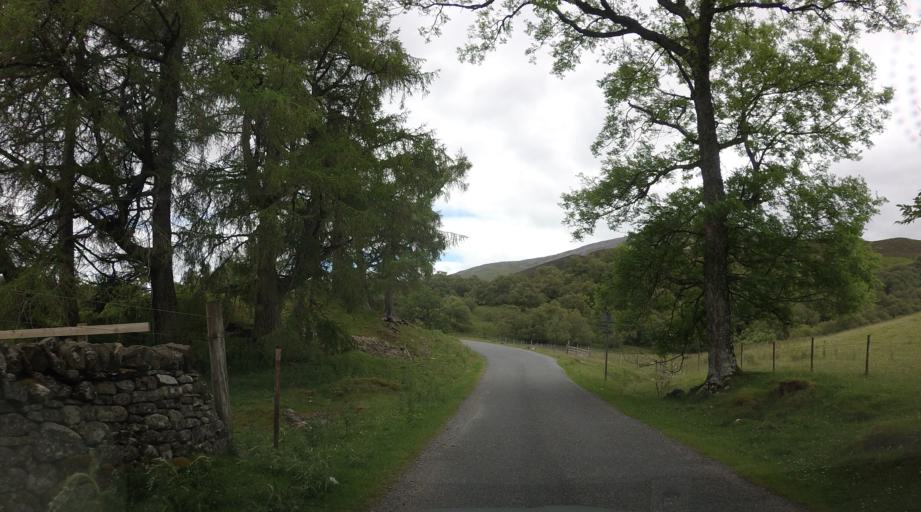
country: GB
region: Scotland
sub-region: Perth and Kinross
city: Aberfeldy
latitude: 56.6920
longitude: -4.1070
